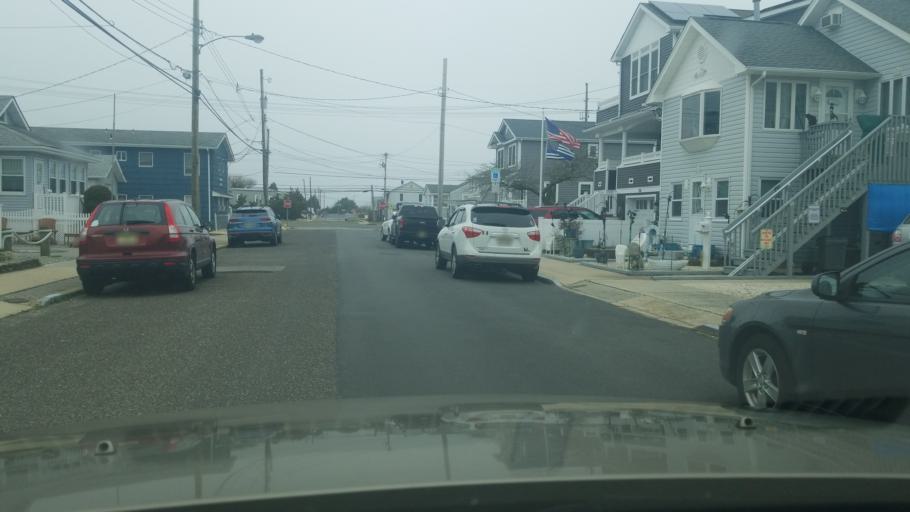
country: US
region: New Jersey
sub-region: Ocean County
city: Seaside Heights
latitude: 39.9365
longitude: -74.0750
